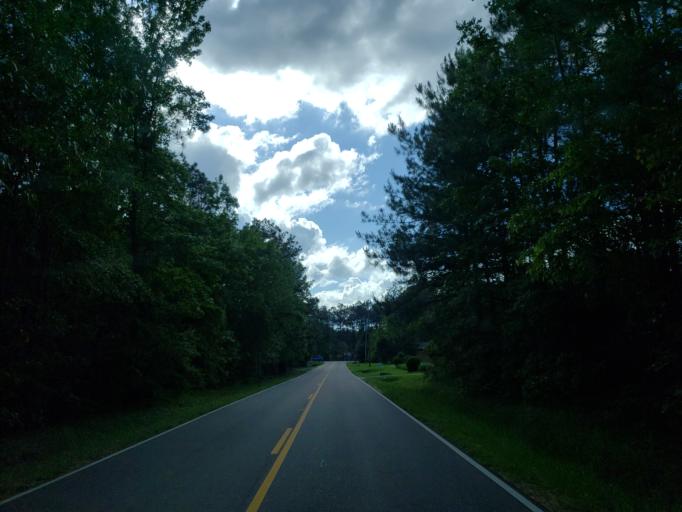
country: US
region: Mississippi
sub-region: Lamar County
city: Sumrall
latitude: 31.3550
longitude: -89.4965
